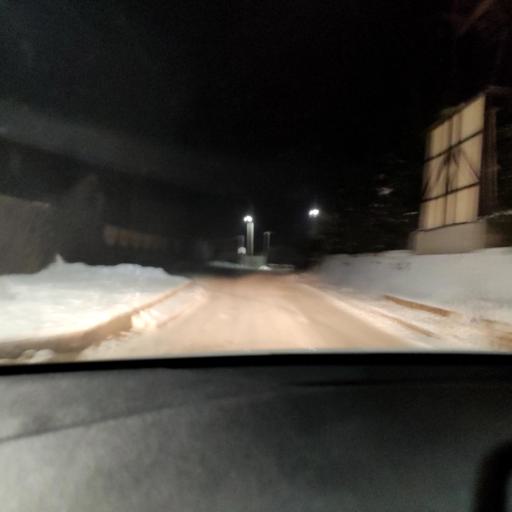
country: RU
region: Tatarstan
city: Stolbishchi
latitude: 55.7556
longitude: 49.2541
